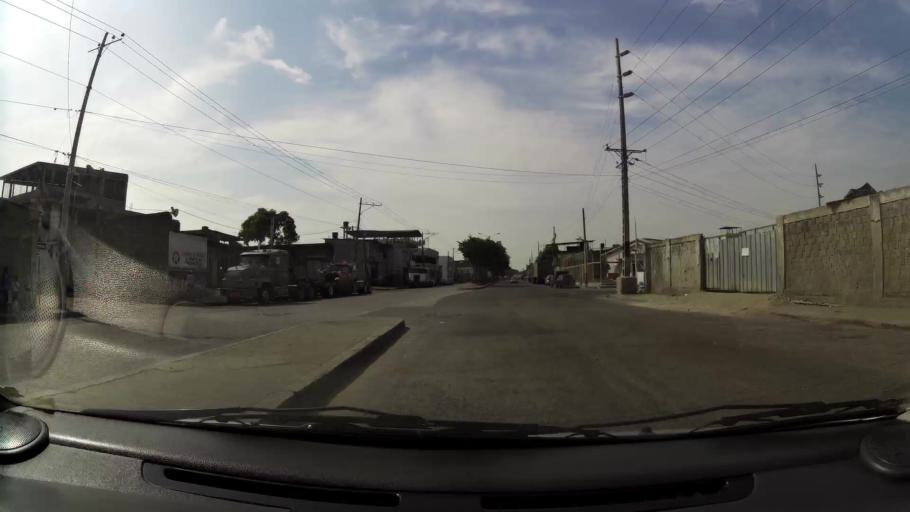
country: EC
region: Guayas
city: Guayaquil
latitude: -2.2757
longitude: -79.8946
